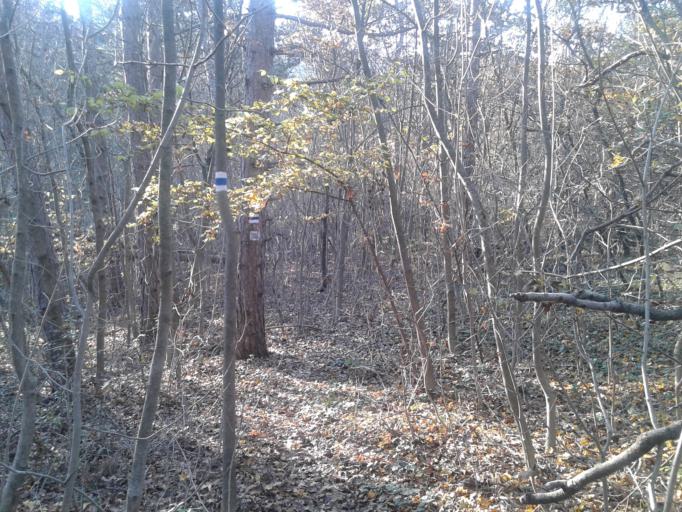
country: HU
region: Fejer
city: Bodajk
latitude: 47.2989
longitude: 18.2344
